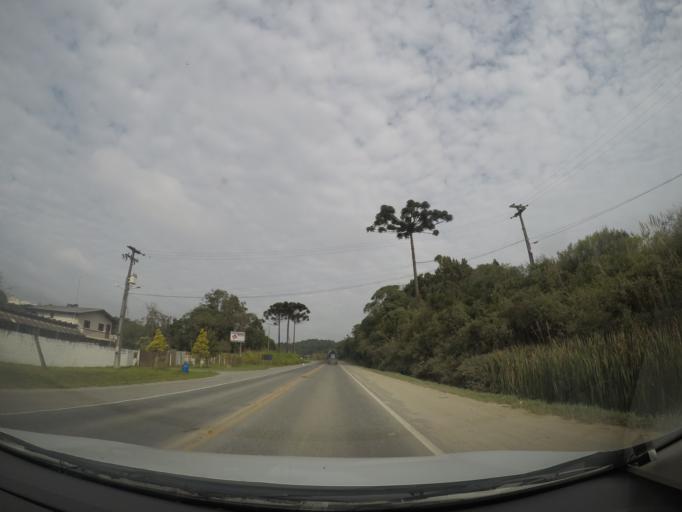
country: BR
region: Parana
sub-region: Almirante Tamandare
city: Almirante Tamandare
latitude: -25.3392
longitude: -49.2594
